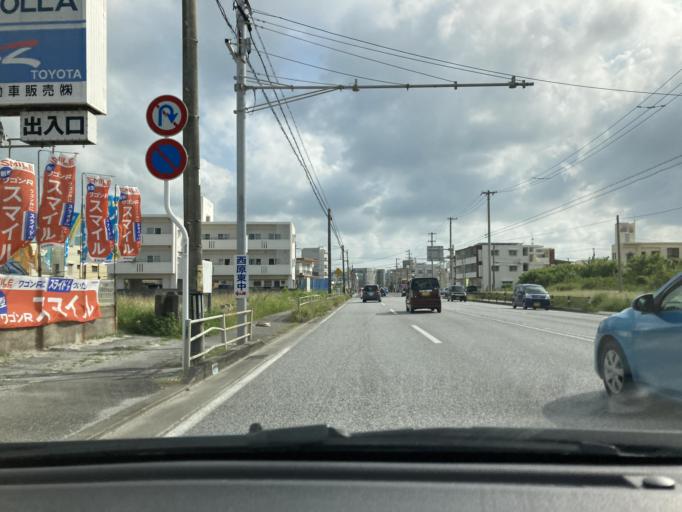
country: JP
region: Okinawa
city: Ginowan
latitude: 26.2234
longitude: 127.7658
